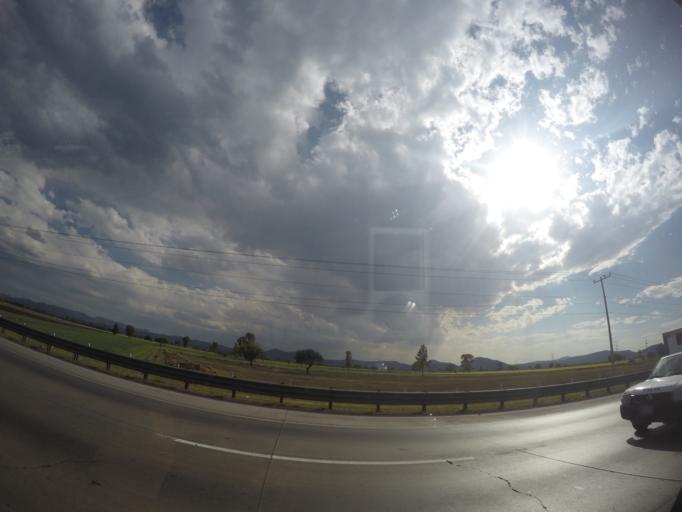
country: MX
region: Queretaro
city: El Sauz
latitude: 20.4695
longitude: -100.1053
